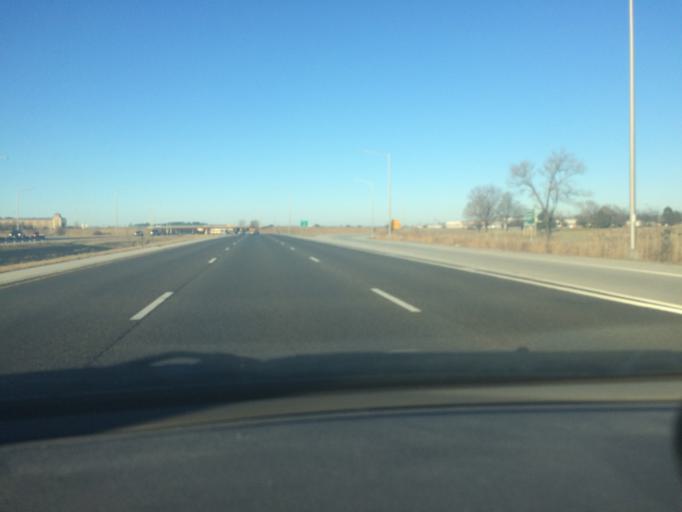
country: US
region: Illinois
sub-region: Cook County
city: Palatine
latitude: 42.1349
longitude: -88.0046
